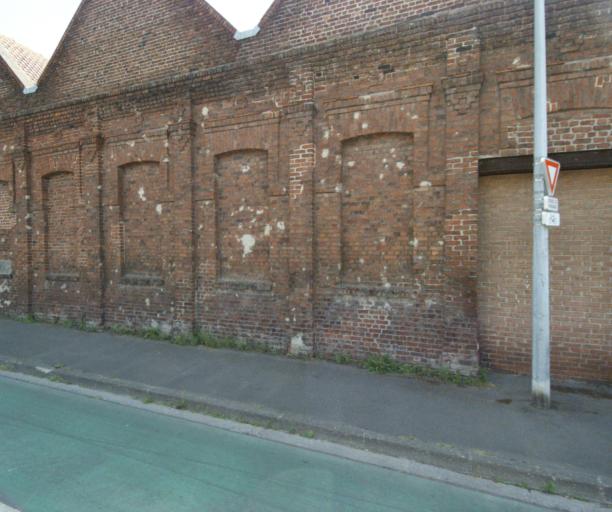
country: FR
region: Nord-Pas-de-Calais
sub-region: Departement du Nord
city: Armentieres
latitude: 50.6920
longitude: 2.8838
